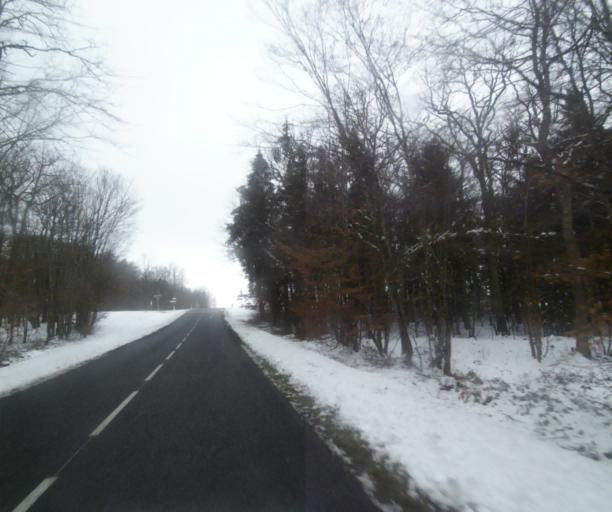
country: FR
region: Champagne-Ardenne
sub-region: Departement de la Haute-Marne
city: Laneuville-a-Remy
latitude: 48.4409
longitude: 4.8583
